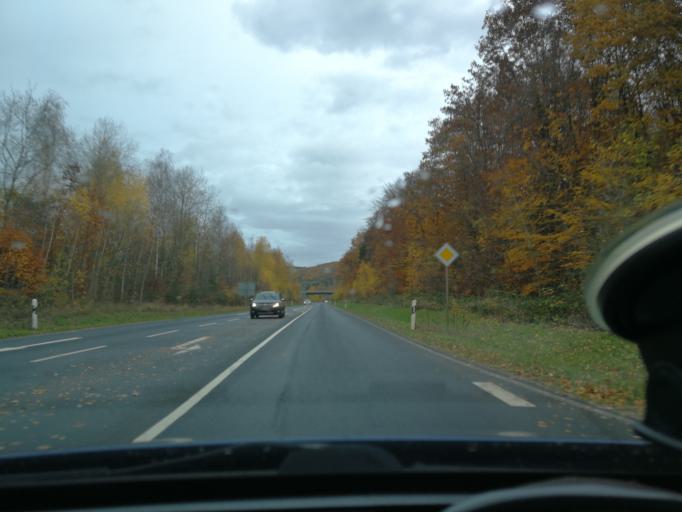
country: DE
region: Rheinland-Pfalz
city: Klausen
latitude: 49.9060
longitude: 6.8731
